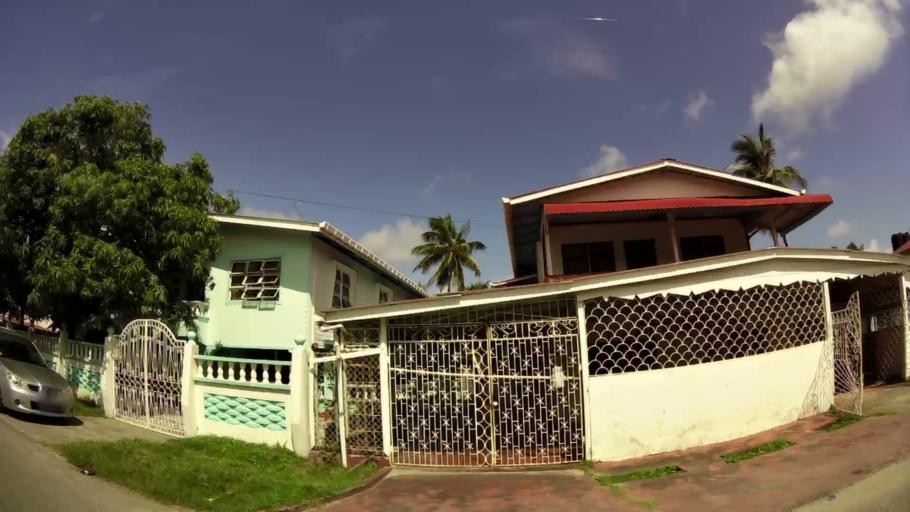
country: GY
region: Demerara-Mahaica
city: Mahaica Village
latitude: 6.7554
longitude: -57.9927
